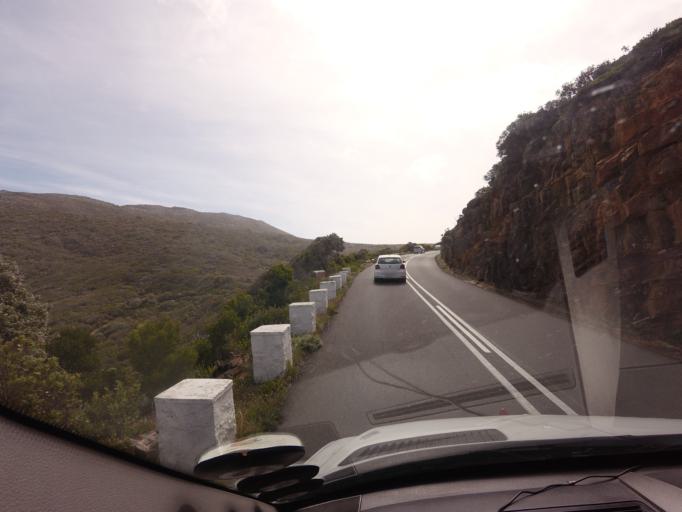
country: ZA
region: Western Cape
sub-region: City of Cape Town
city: Retreat
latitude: -34.2614
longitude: 18.4675
